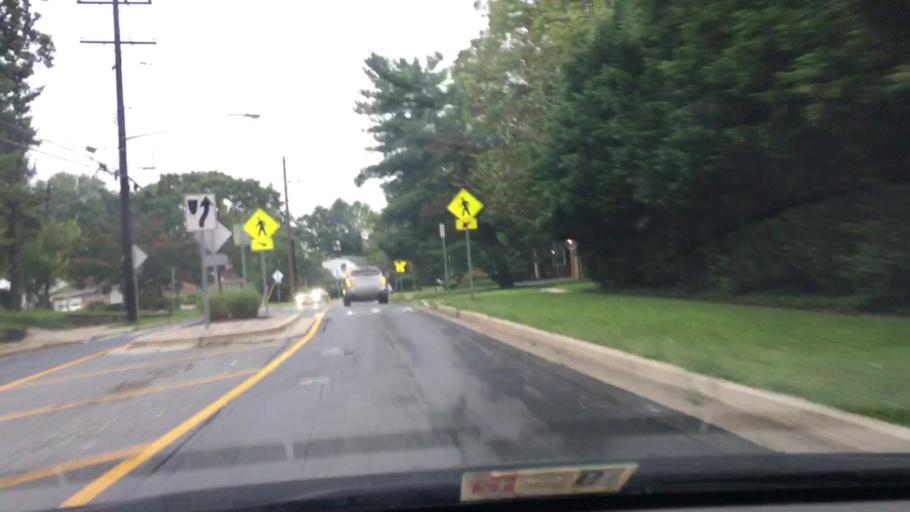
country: US
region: Maryland
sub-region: Montgomery County
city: Rockville
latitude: 39.0763
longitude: -77.1318
